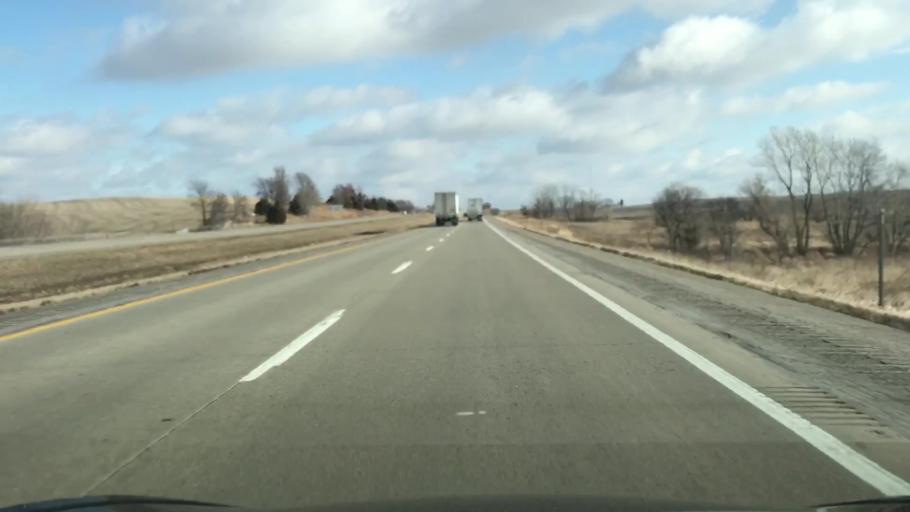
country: US
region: Iowa
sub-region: Cass County
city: Atlantic
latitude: 41.4972
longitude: -94.9885
